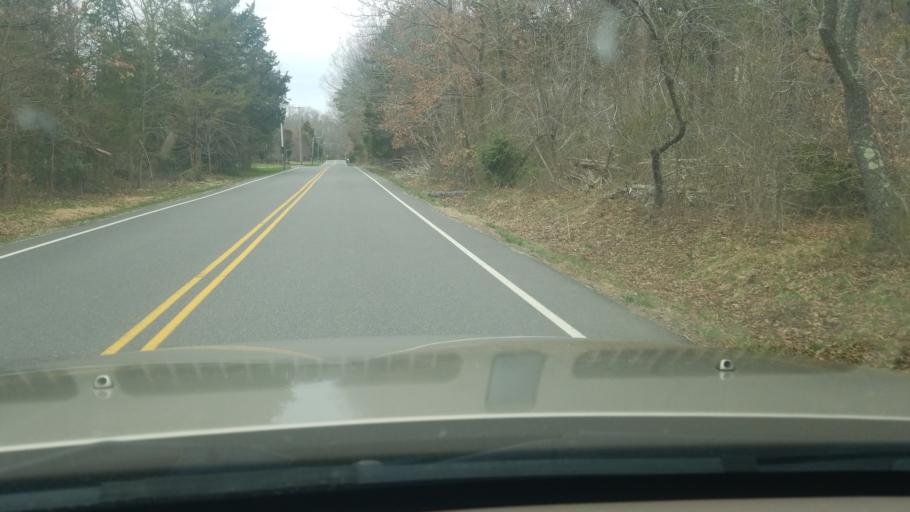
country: US
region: New Jersey
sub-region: Ocean County
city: Lakewood
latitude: 40.1154
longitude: -74.2037
